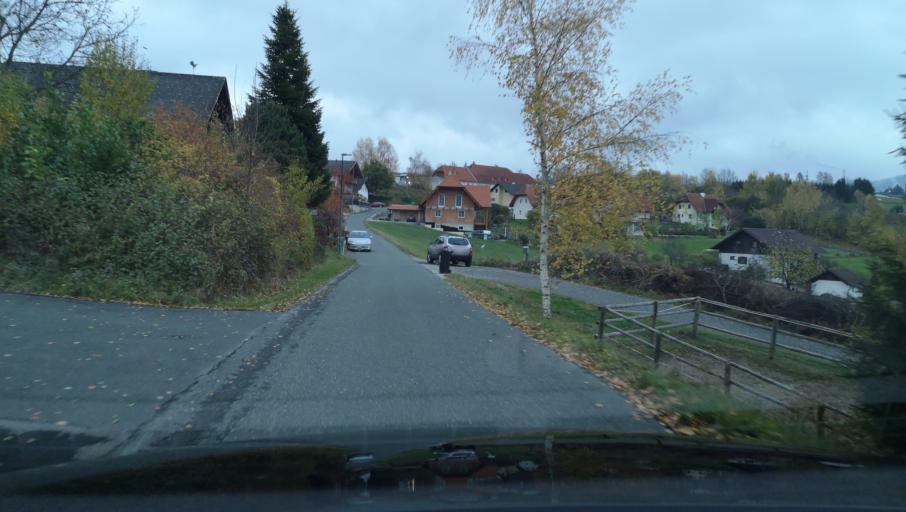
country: AT
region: Styria
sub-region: Politischer Bezirk Weiz
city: Birkfeld
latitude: 47.3492
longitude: 15.6865
